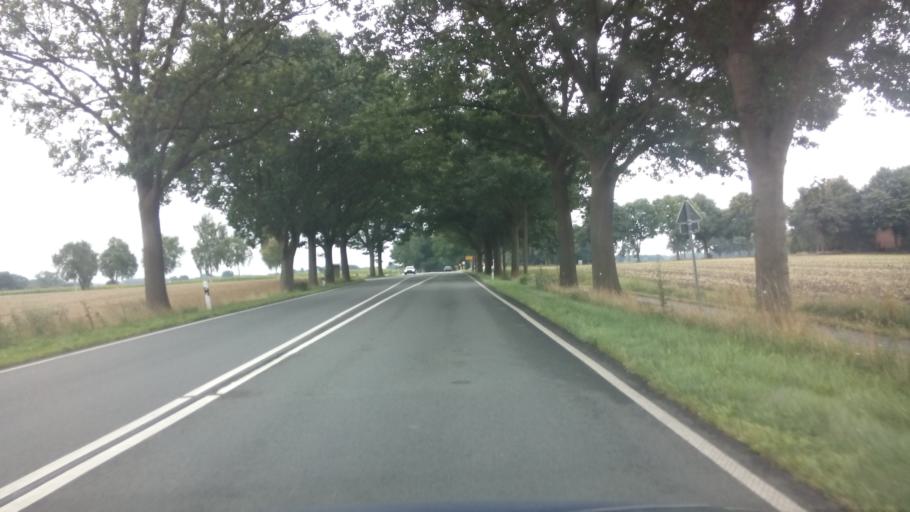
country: DE
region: Lower Saxony
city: Bassum
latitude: 52.9046
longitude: 8.7250
